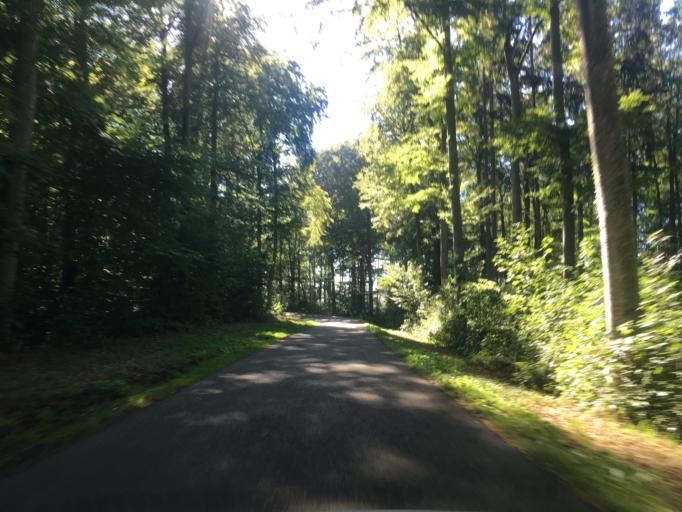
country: DE
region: Baden-Wuerttemberg
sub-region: Tuebingen Region
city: Pfullingen
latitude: 48.4154
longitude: 9.2189
